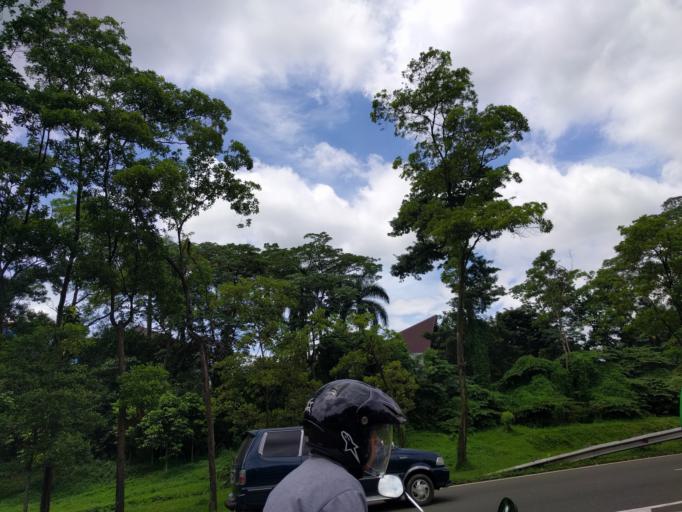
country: ID
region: West Java
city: Bogor
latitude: -6.6019
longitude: 106.8109
